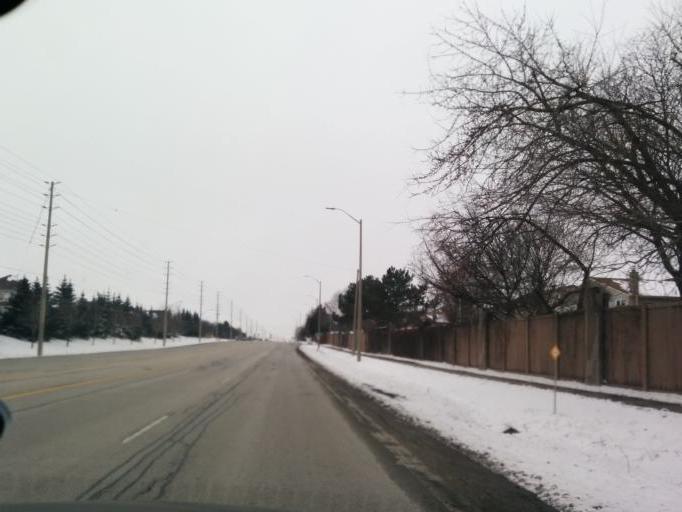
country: CA
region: Ontario
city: Mississauga
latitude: 43.5723
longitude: -79.7403
